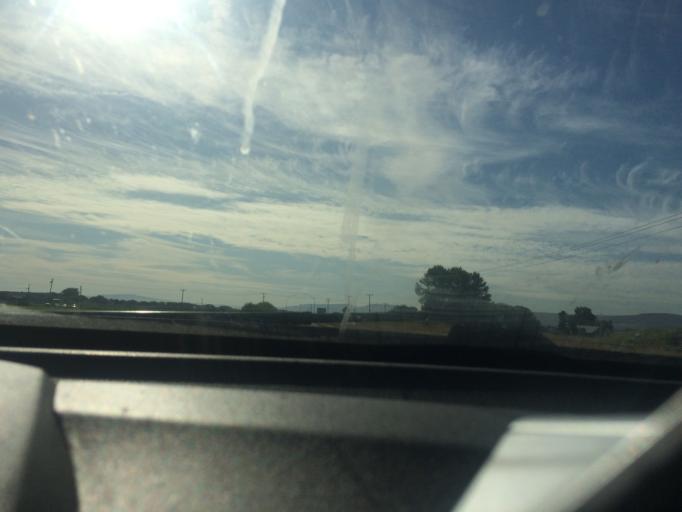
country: US
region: Washington
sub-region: Kittitas County
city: Ellensburg
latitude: 47.0240
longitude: -120.5956
